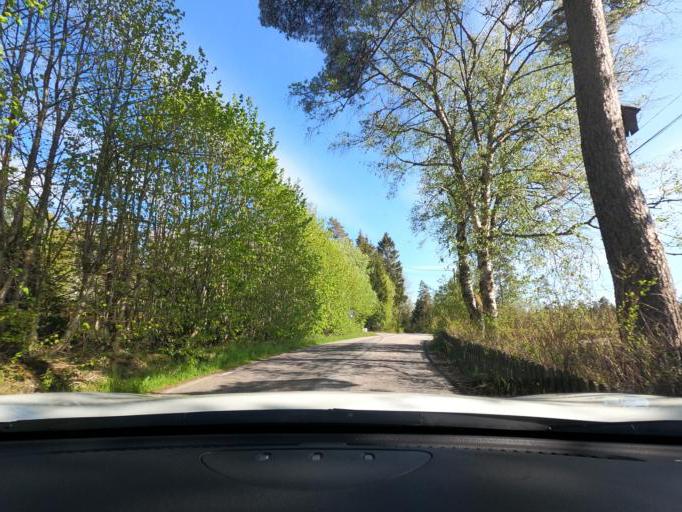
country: SE
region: Vaestra Goetaland
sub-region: Harryda Kommun
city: Hindas
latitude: 57.6714
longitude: 12.3512
